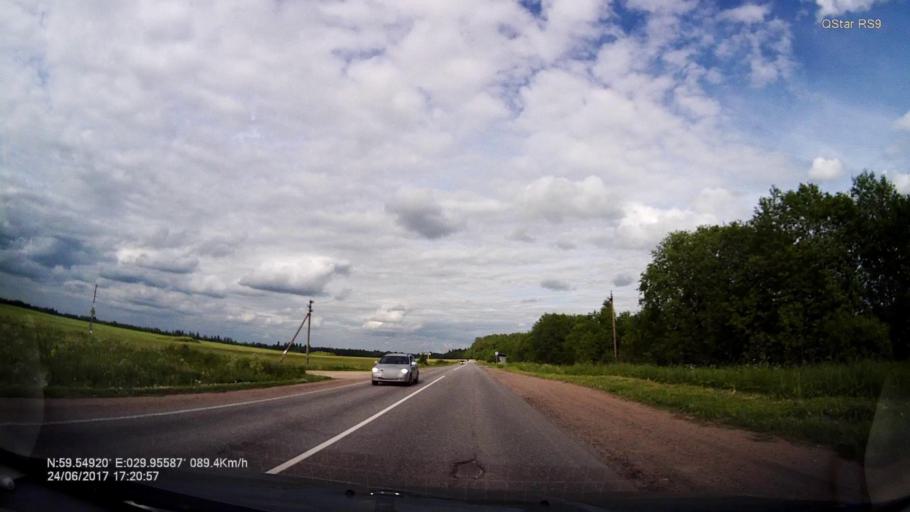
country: RU
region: Leningrad
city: Voyskovitsy
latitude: 59.5494
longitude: 29.9569
